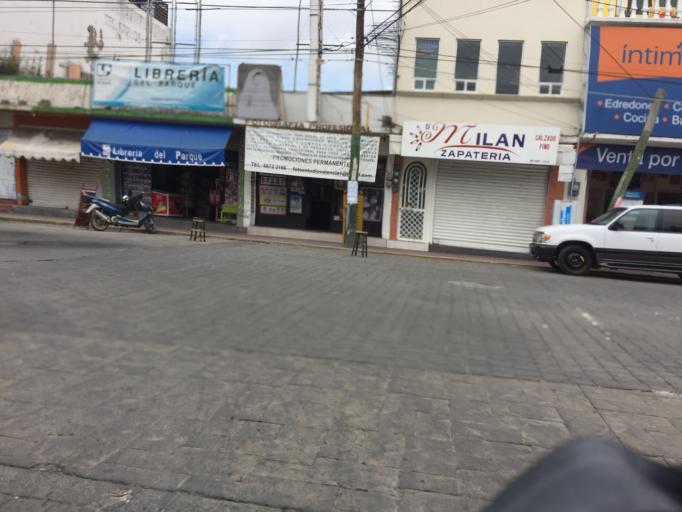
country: MX
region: Mexico
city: Cuautitlan
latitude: 19.6697
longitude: -99.1804
